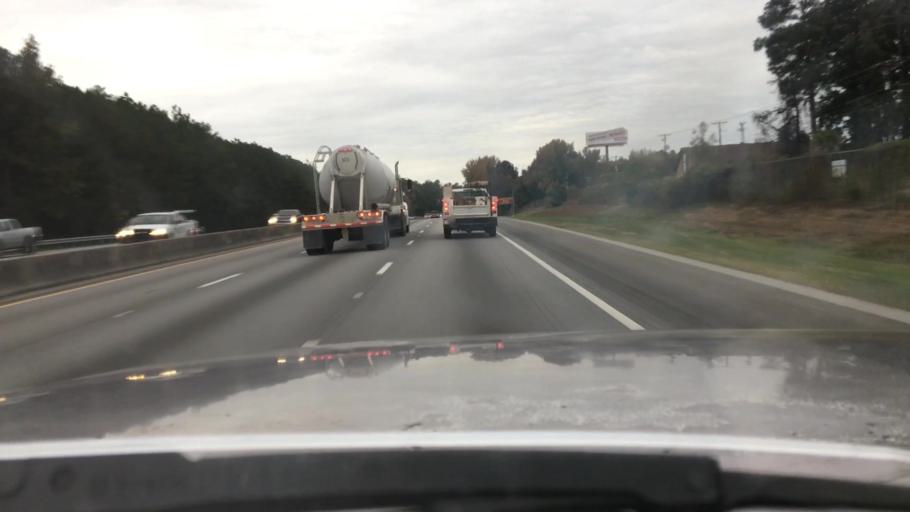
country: US
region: South Carolina
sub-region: Lexington County
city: Saint Andrews
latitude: 34.0179
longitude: -81.1382
